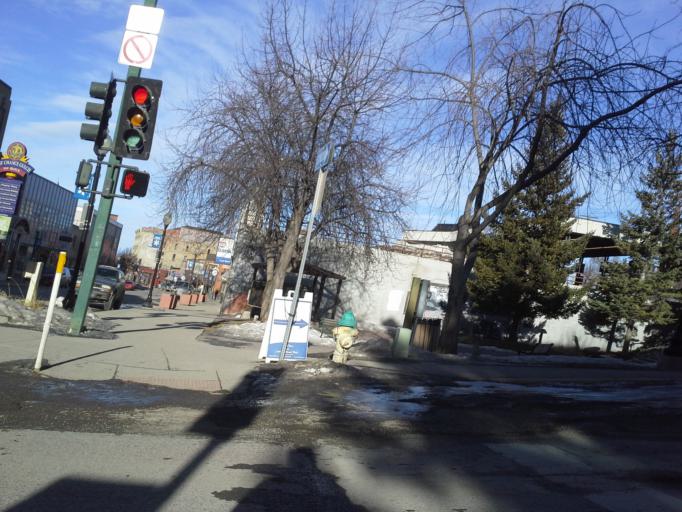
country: US
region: Montana
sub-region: Lewis and Clark County
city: Helena
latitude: 46.5887
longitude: -112.0385
